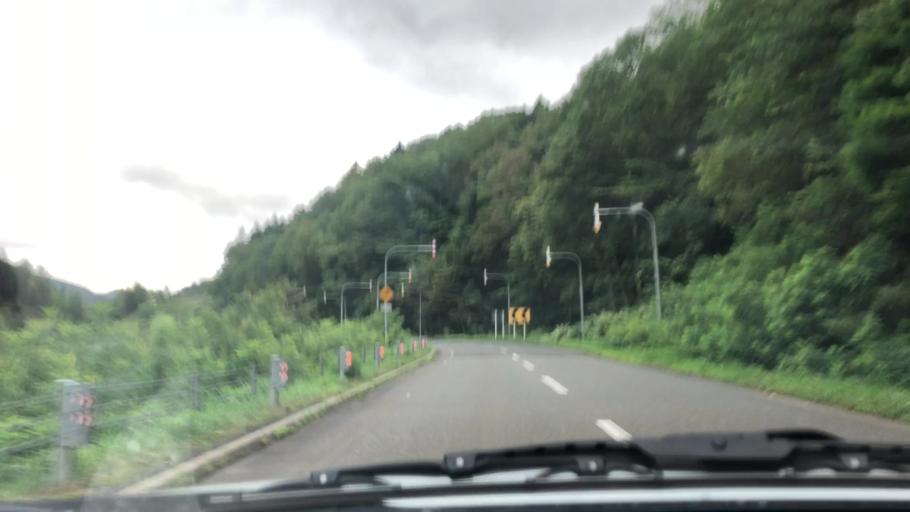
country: JP
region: Hokkaido
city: Shimo-furano
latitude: 42.9392
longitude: 142.3735
